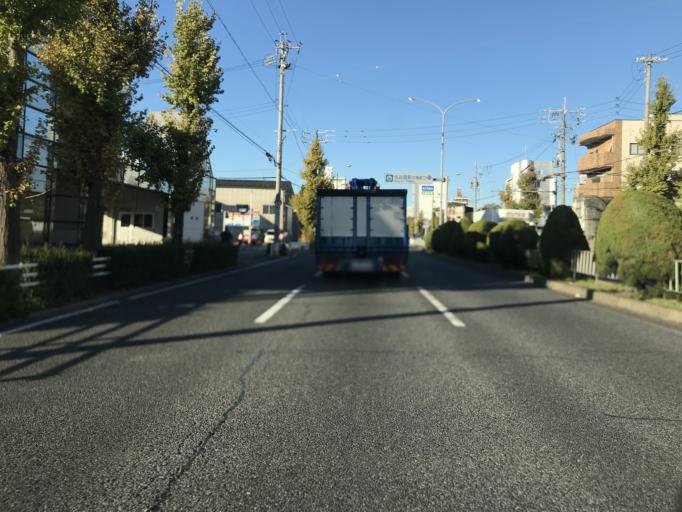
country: JP
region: Aichi
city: Nagoya-shi
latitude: 35.1712
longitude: 136.8728
